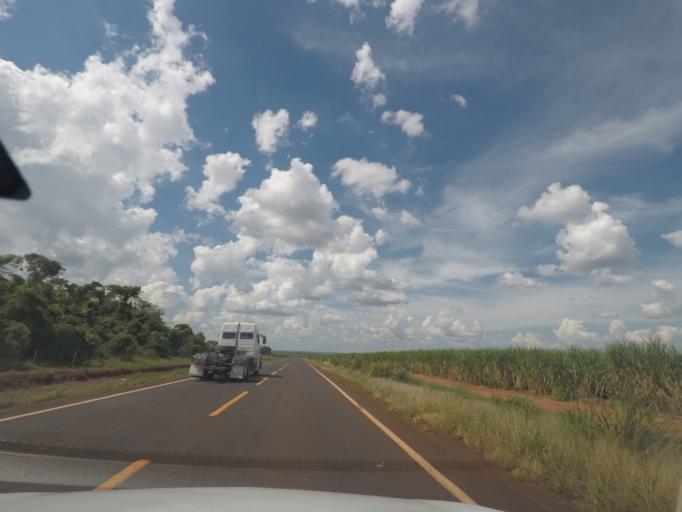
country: BR
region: Minas Gerais
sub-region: Conceicao Das Alagoas
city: Conceicao das Alagoas
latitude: -19.8474
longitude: -48.5961
